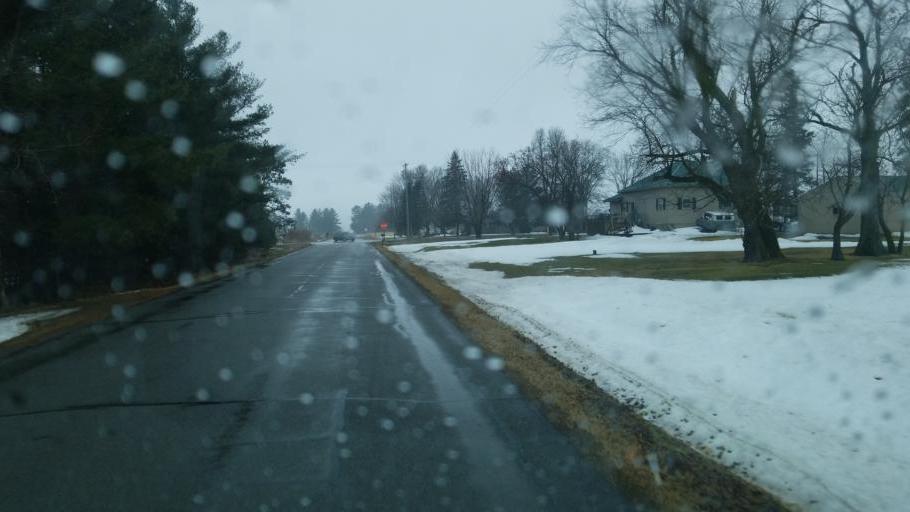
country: US
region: Wisconsin
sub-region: Marathon County
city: Spencer
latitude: 44.6574
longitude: -90.2792
